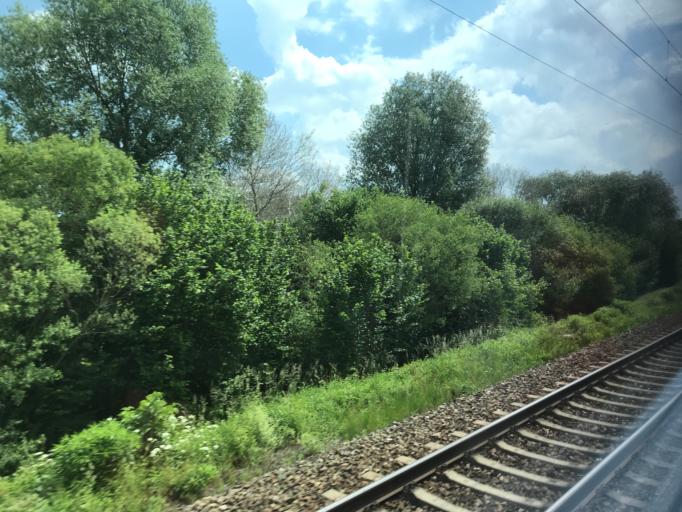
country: DE
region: Bavaria
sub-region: Swabia
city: Offingen
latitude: 48.4846
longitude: 10.3726
